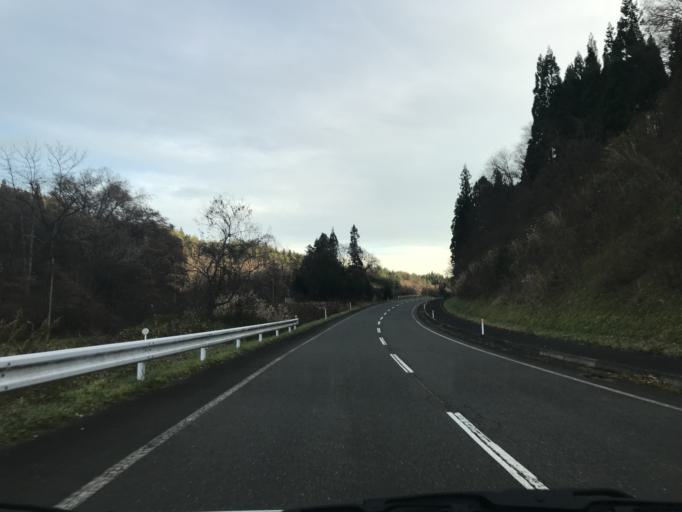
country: JP
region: Iwate
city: Ichinoseki
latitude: 38.9941
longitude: 141.0654
